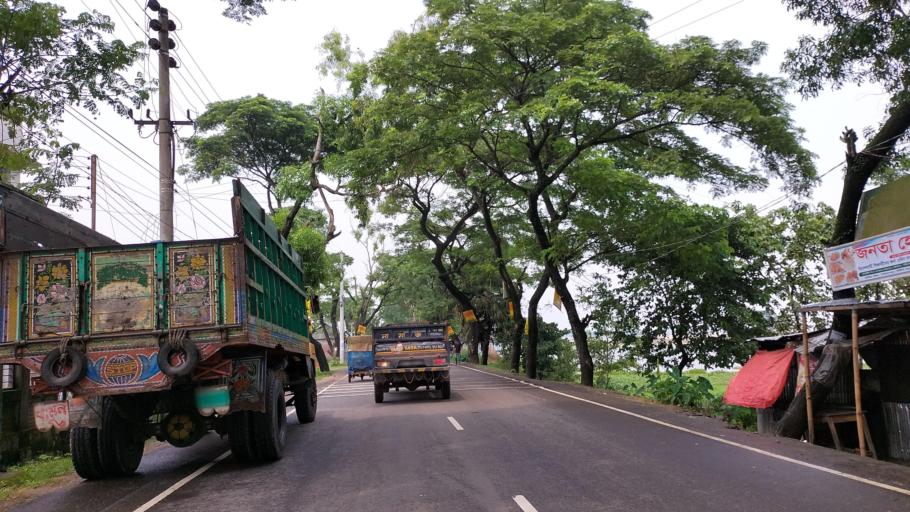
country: BD
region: Dhaka
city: Netrakona
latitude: 24.8970
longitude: 90.7465
